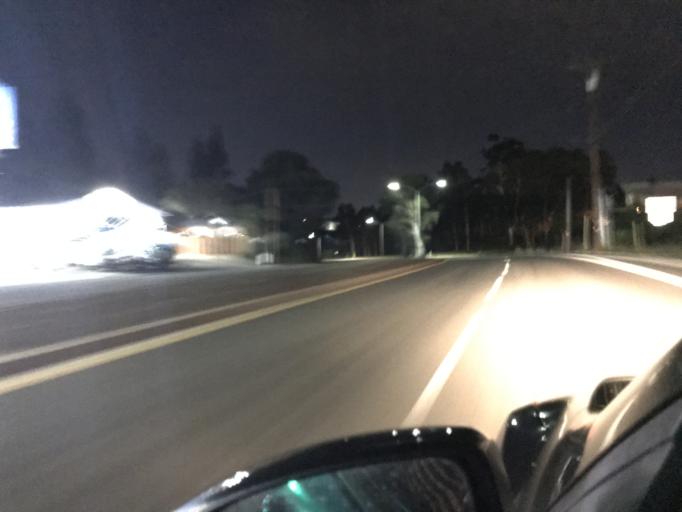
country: US
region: California
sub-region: San Diego County
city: La Mesa
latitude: 32.7794
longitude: -117.0406
